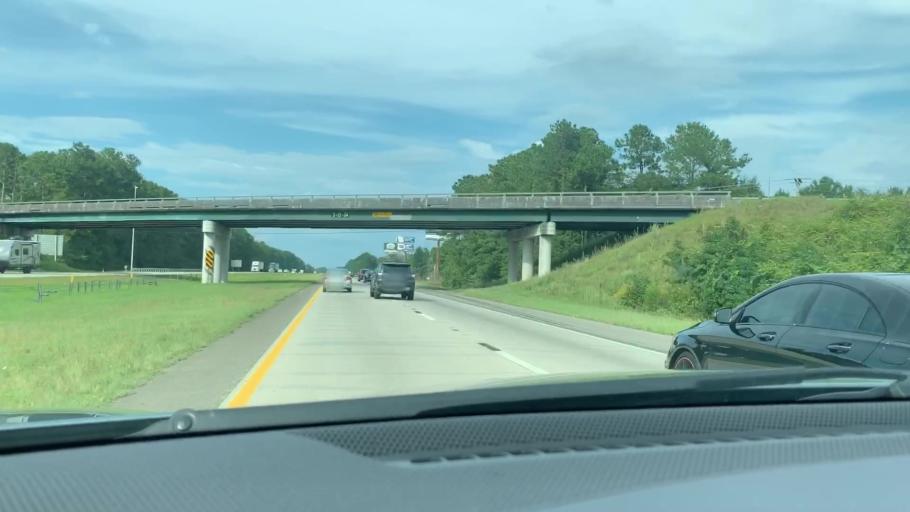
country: US
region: South Carolina
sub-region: Colleton County
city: Walterboro
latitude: 32.9410
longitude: -80.6851
